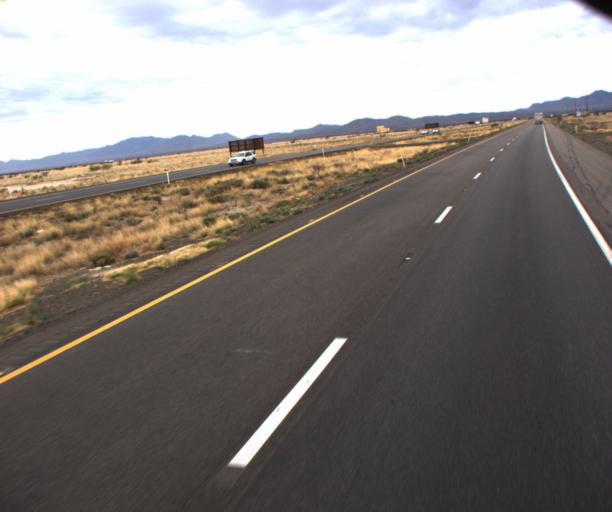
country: US
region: Arizona
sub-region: Cochise County
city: Willcox
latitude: 32.2147
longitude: -109.8857
